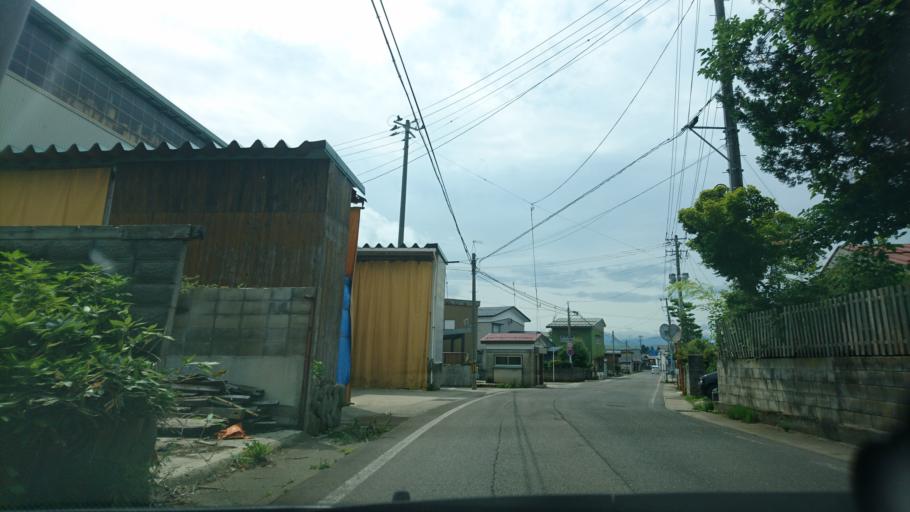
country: JP
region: Akita
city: Yuzawa
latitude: 39.1980
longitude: 140.5468
